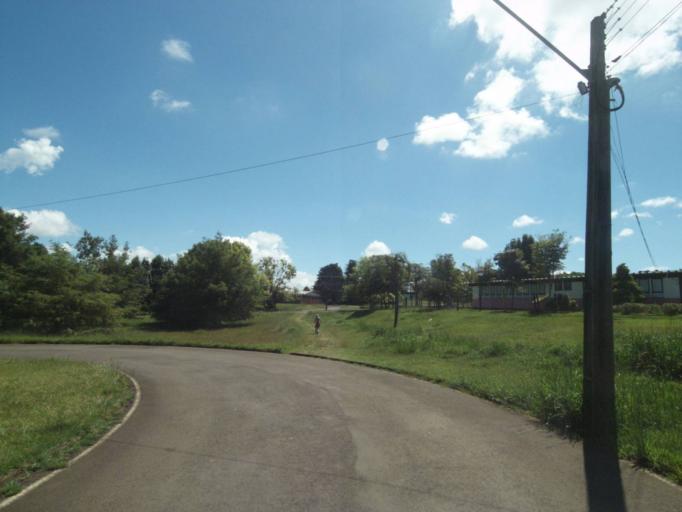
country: BR
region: Parana
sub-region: Pinhao
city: Pinhao
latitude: -25.7932
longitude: -52.0858
